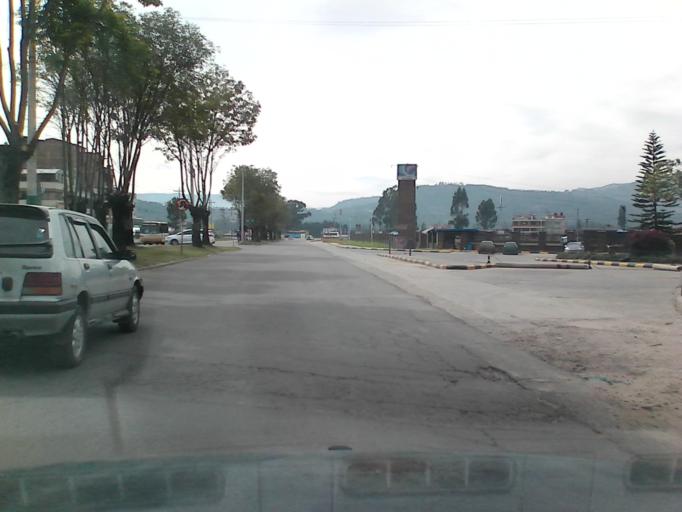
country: CO
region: Boyaca
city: Duitama
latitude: 5.8096
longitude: -73.0291
